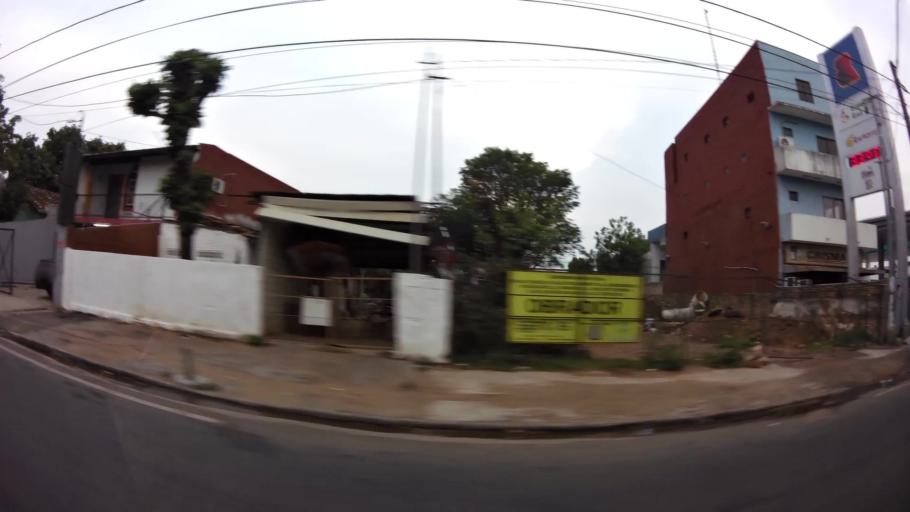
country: PY
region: Asuncion
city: Asuncion
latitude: -25.3188
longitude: -57.6209
